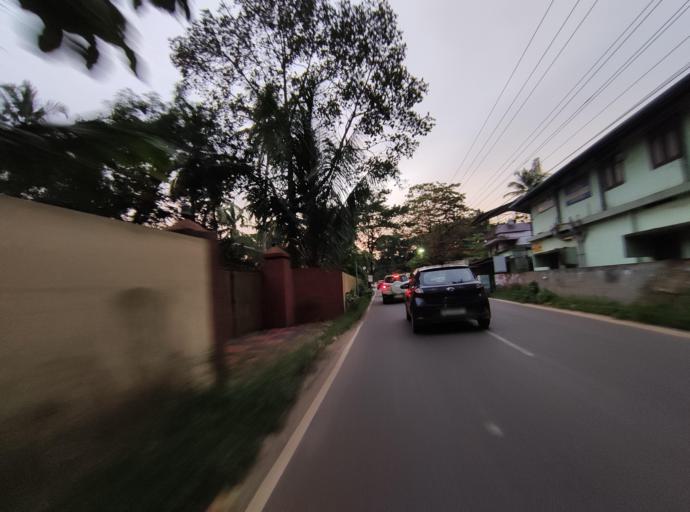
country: IN
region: Kerala
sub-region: Alappuzha
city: Shertallai
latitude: 9.6847
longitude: 76.3523
